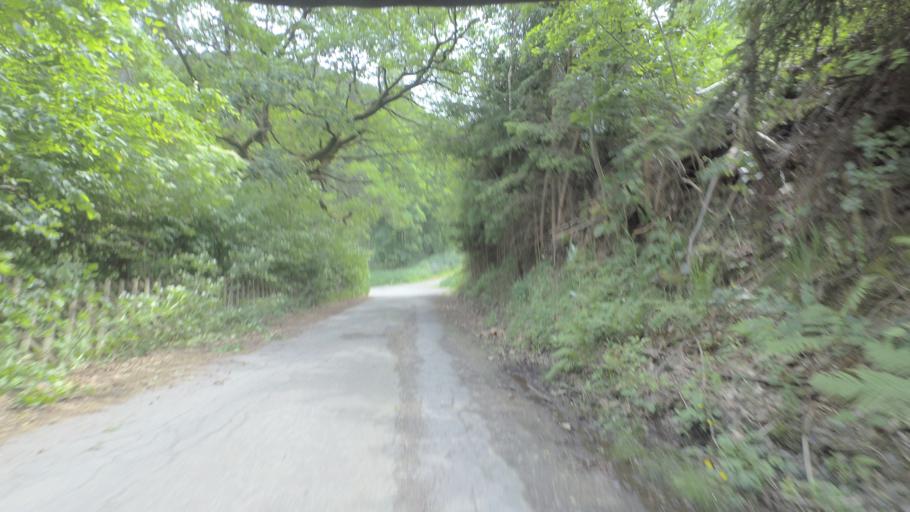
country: DE
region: Lower Saxony
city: Goslar
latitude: 51.8959
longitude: 10.4621
